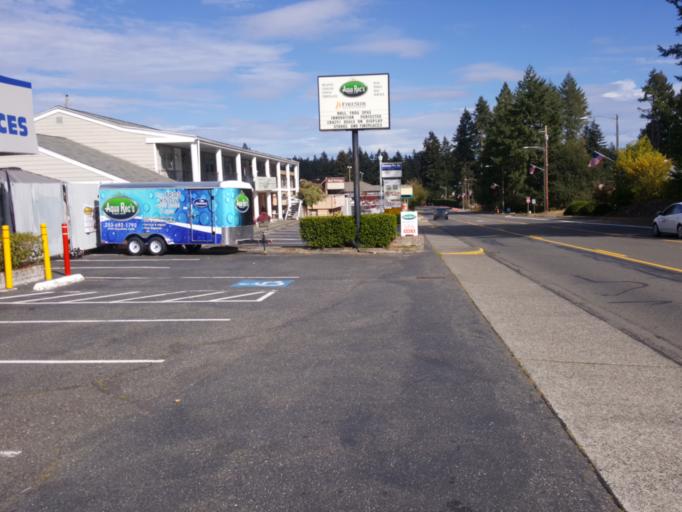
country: US
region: Washington
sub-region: Pierce County
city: Fircrest
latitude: 47.2389
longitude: -122.5212
